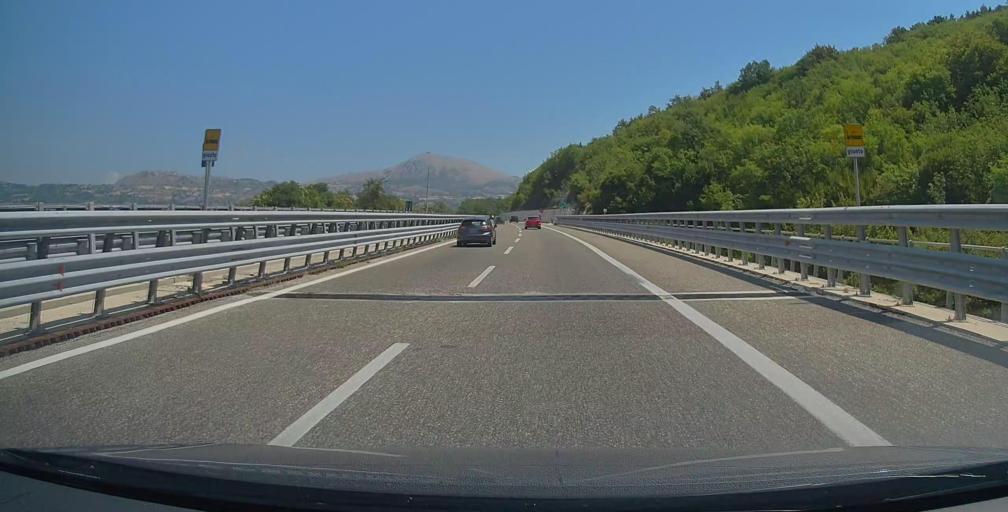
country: IT
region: Campania
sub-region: Provincia di Salerno
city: Pertosa
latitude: 40.5315
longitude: 15.4549
